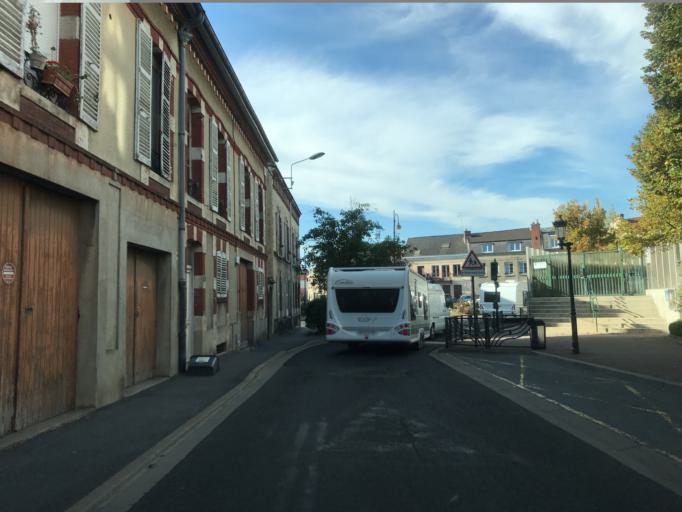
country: FR
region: Champagne-Ardenne
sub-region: Departement de la Marne
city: Epernay
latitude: 49.0469
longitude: 3.9515
